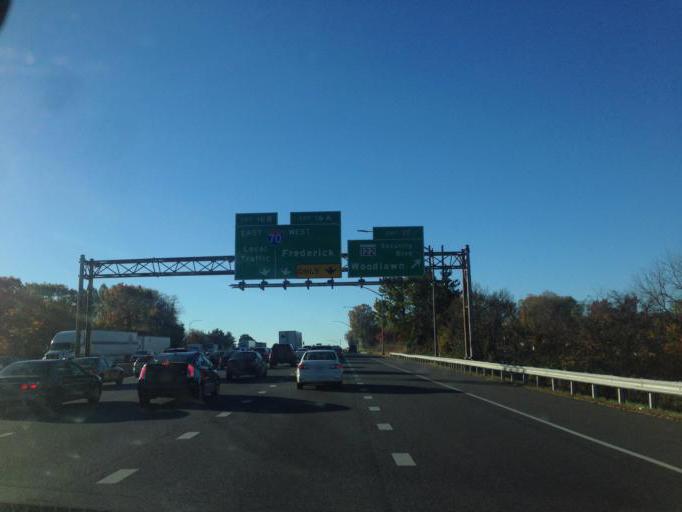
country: US
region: Maryland
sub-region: Baltimore County
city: Woodlawn
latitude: 39.3175
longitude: -76.7449
